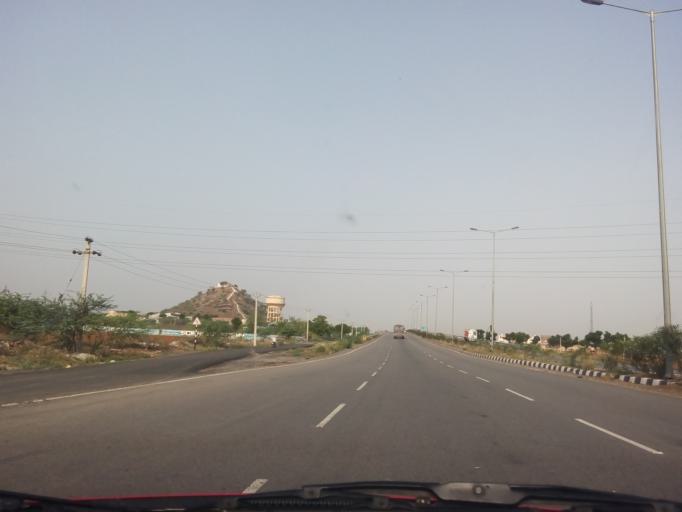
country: IN
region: Rajasthan
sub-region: Ajmer
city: Kishangarh
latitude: 26.5509
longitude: 74.7790
